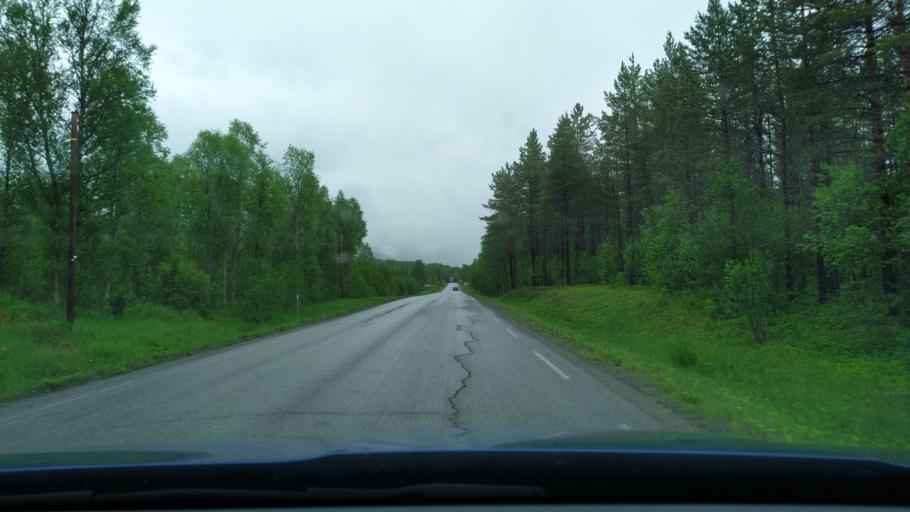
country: NO
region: Troms
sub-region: Dyroy
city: Brostadbotn
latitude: 69.0679
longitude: 17.7352
